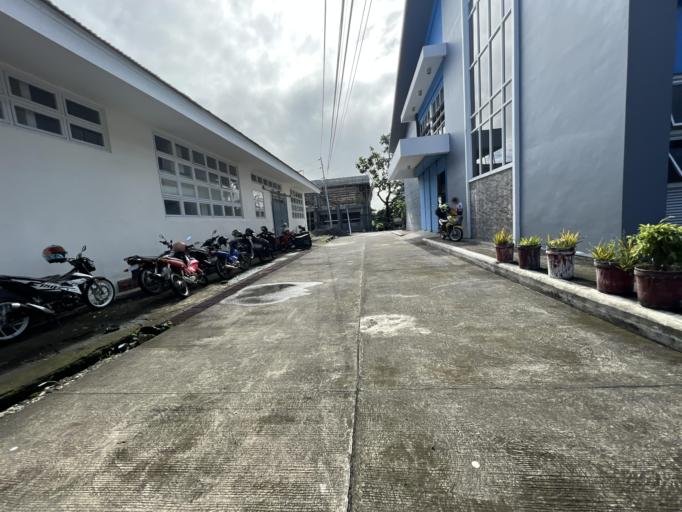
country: PH
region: Bicol
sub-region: Province of Albay
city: Sagpon
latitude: 13.1471
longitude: 123.7293
